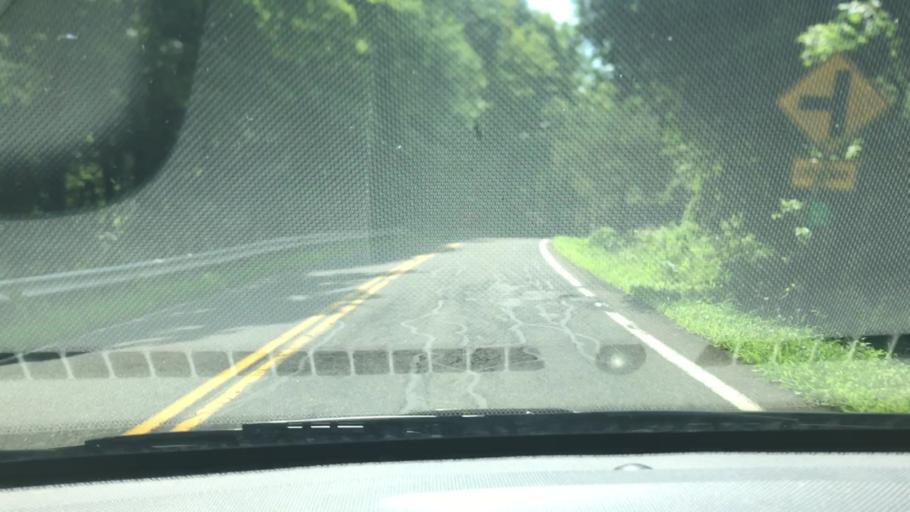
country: US
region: New York
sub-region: Ulster County
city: Stone Ridge
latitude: 41.9021
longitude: -74.1689
